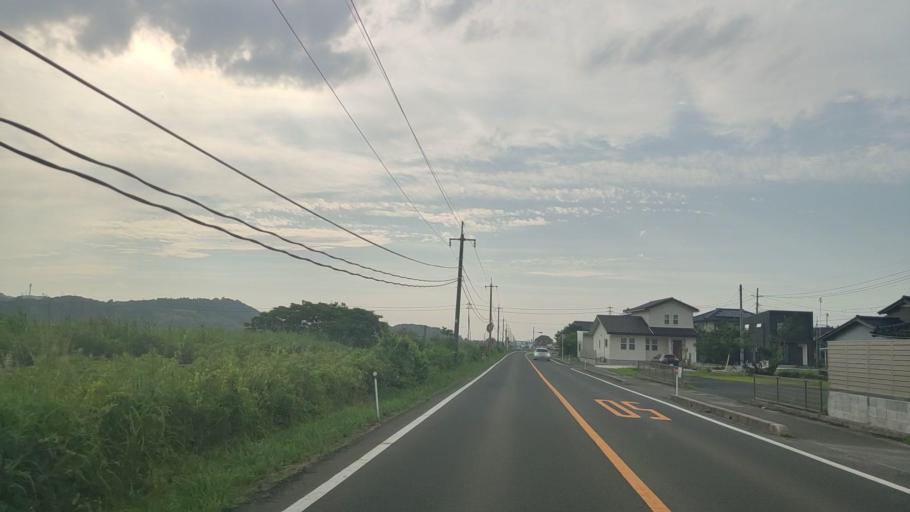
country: JP
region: Tottori
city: Kurayoshi
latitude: 35.4749
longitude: 133.8224
